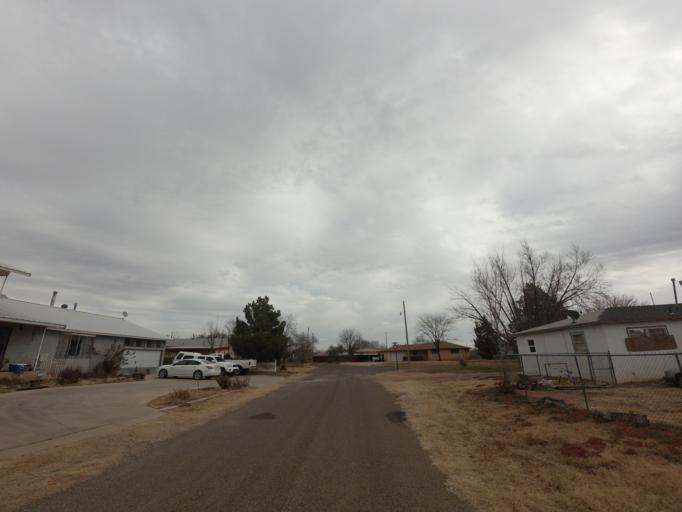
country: US
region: New Mexico
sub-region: Curry County
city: Clovis
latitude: 34.3815
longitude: -103.2012
